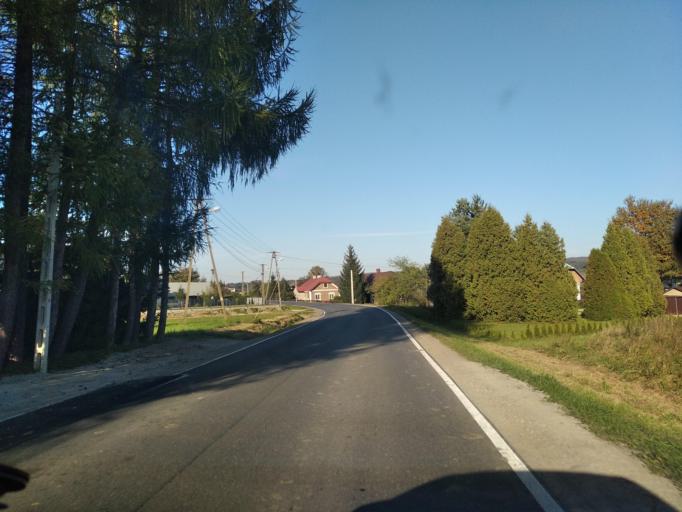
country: PL
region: Subcarpathian Voivodeship
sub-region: Powiat brzozowski
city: Humniska
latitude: 49.6737
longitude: 22.0314
